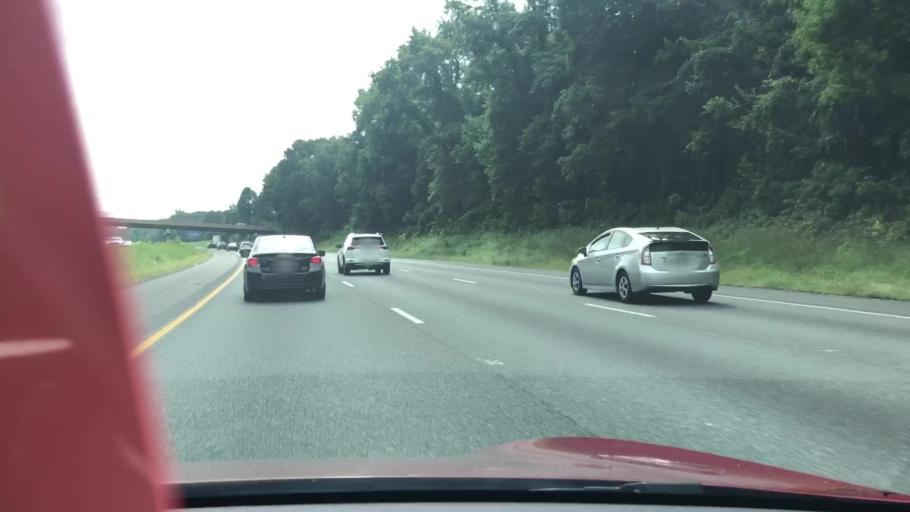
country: US
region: Maryland
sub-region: Harford County
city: Havre de Grace
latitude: 39.5729
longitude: -76.1366
